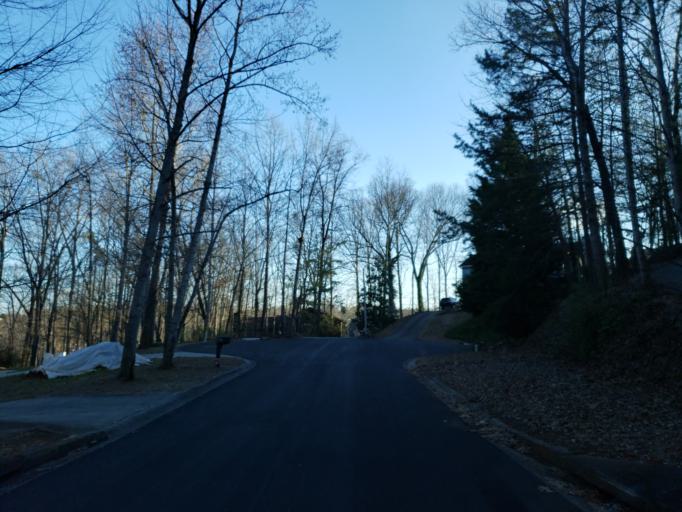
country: US
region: Georgia
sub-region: Cherokee County
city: Woodstock
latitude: 34.0518
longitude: -84.4815
